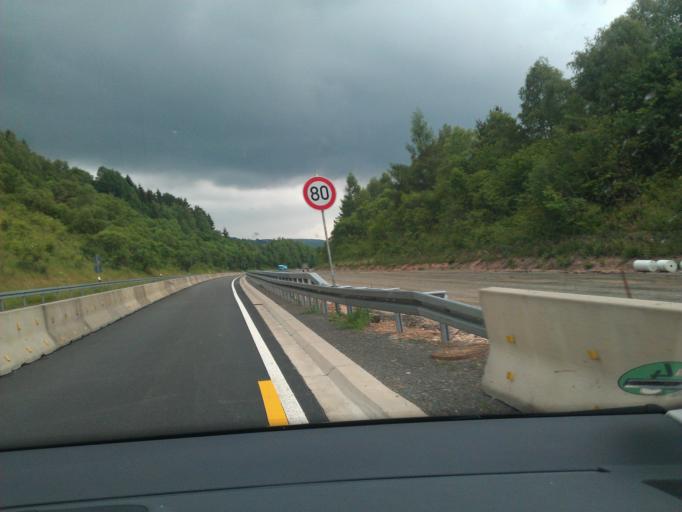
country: DE
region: Rheinland-Pfalz
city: Neuhutten
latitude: 49.5919
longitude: 7.0258
